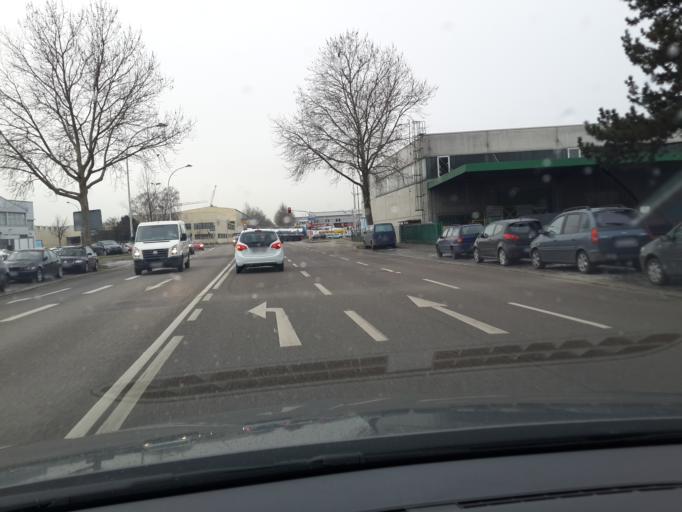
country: DE
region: Baden-Wuerttemberg
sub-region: Regierungsbezirk Stuttgart
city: Neckarsulm
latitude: 49.1703
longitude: 9.2188
